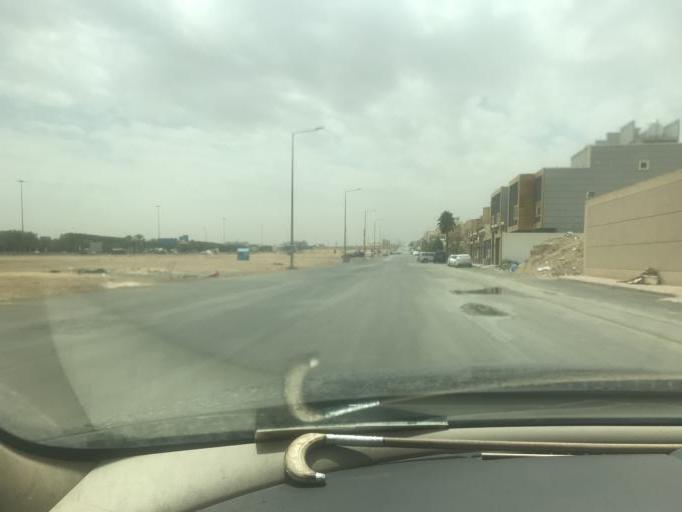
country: SA
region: Ar Riyad
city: Riyadh
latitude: 24.7914
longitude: 46.7156
